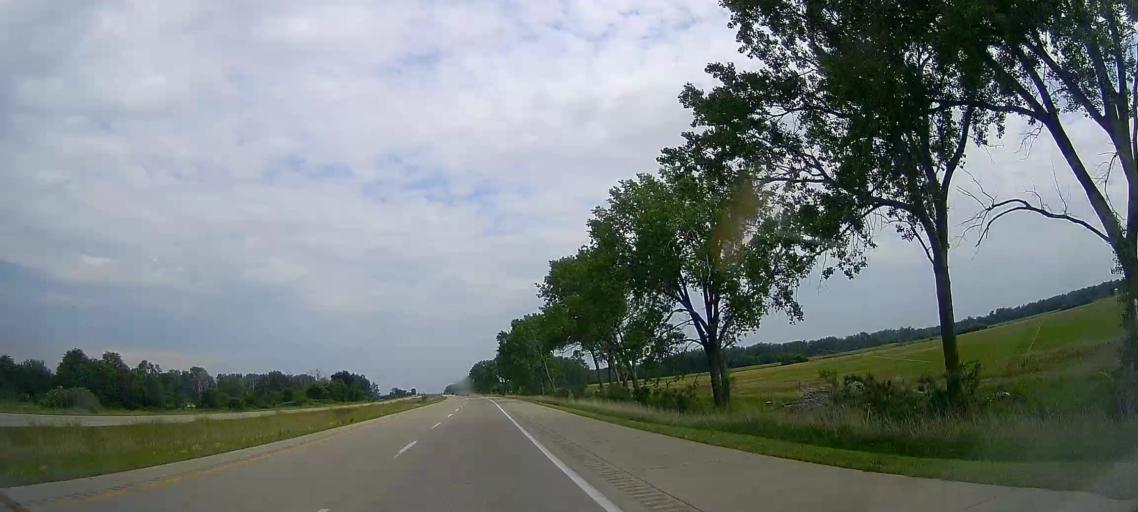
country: US
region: Nebraska
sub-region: Burt County
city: Tekamah
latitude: 41.8247
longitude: -96.0763
